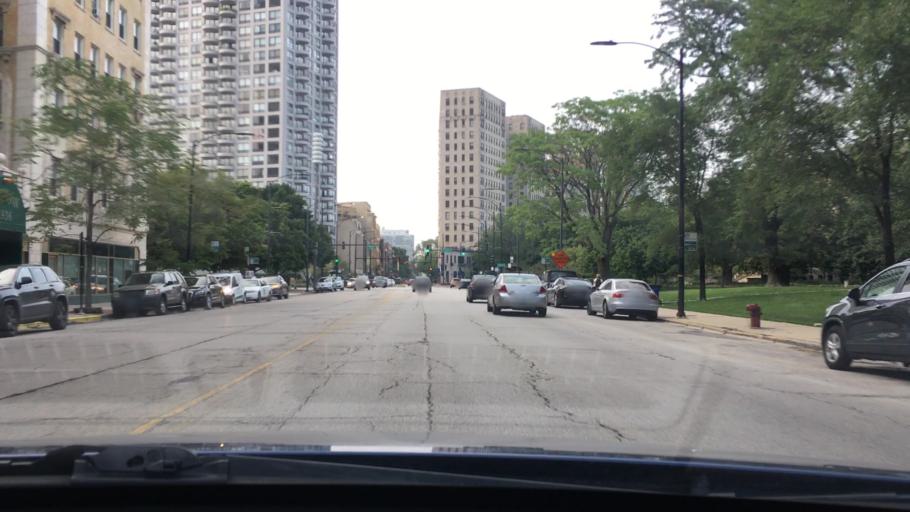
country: US
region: Illinois
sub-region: Cook County
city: Chicago
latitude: 41.9175
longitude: -87.6355
